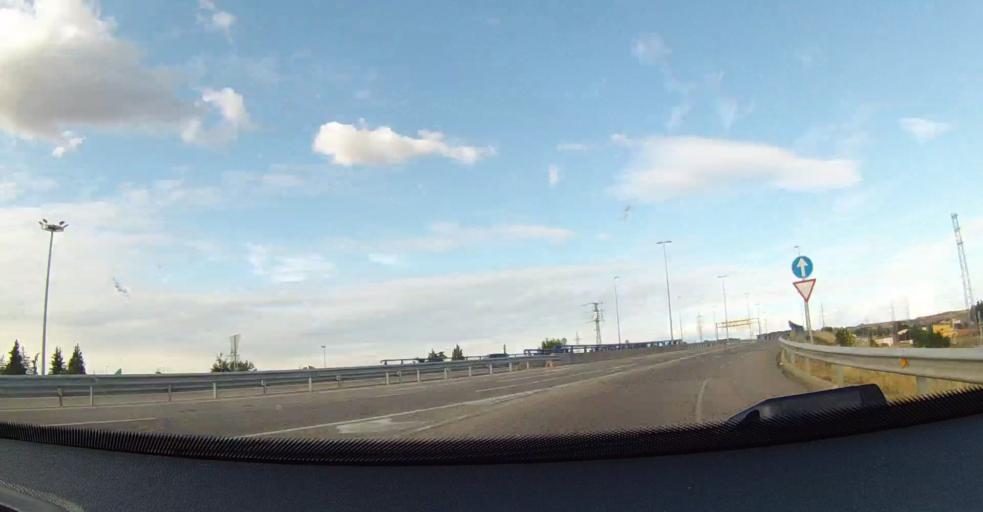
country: ES
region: Castille and Leon
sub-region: Provincia de Leon
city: Leon
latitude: 42.5689
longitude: -5.5831
